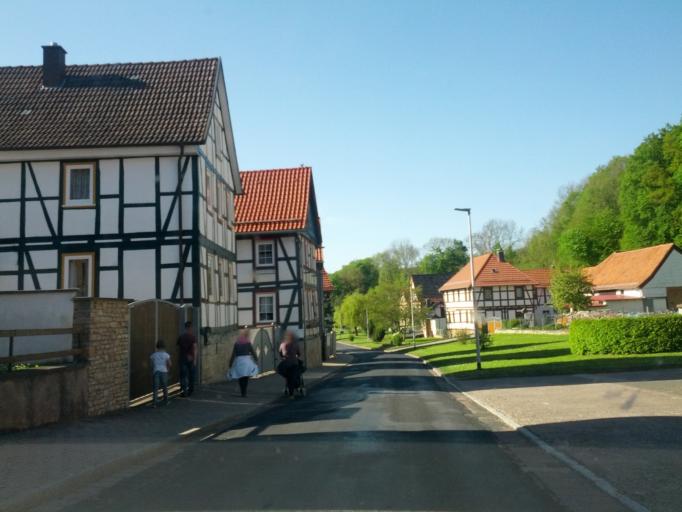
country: DE
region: Hesse
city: Wanfried
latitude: 51.2024
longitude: 10.2123
